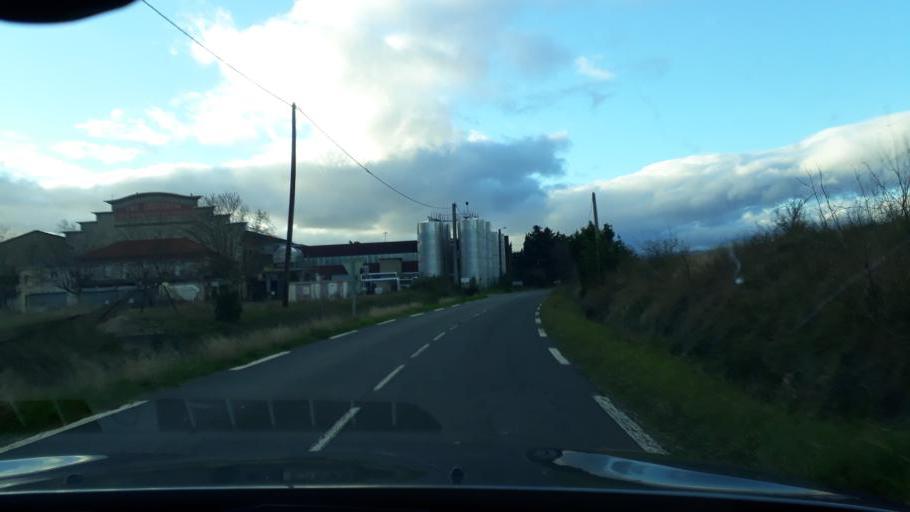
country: FR
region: Languedoc-Roussillon
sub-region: Departement de l'Herault
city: Nissan-lez-Enserune
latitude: 43.2920
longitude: 3.1193
